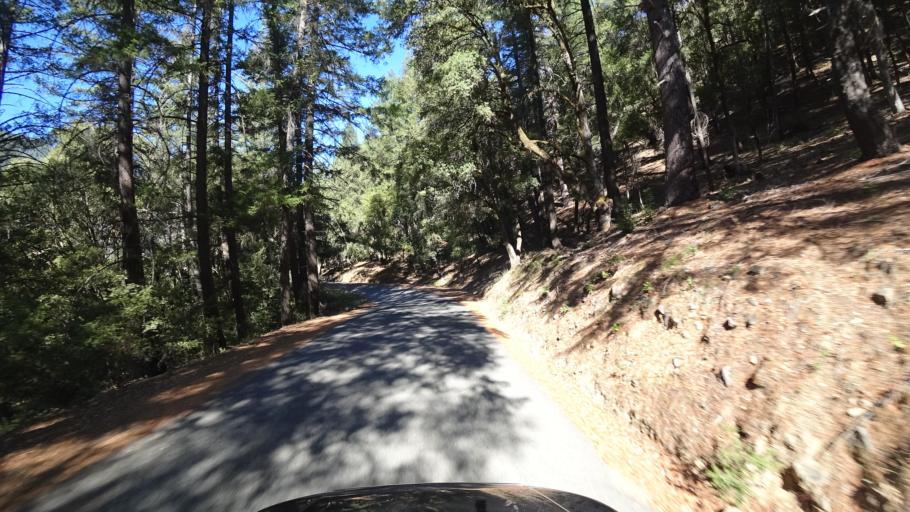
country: US
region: California
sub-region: Humboldt County
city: Willow Creek
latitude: 41.2635
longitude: -123.3296
